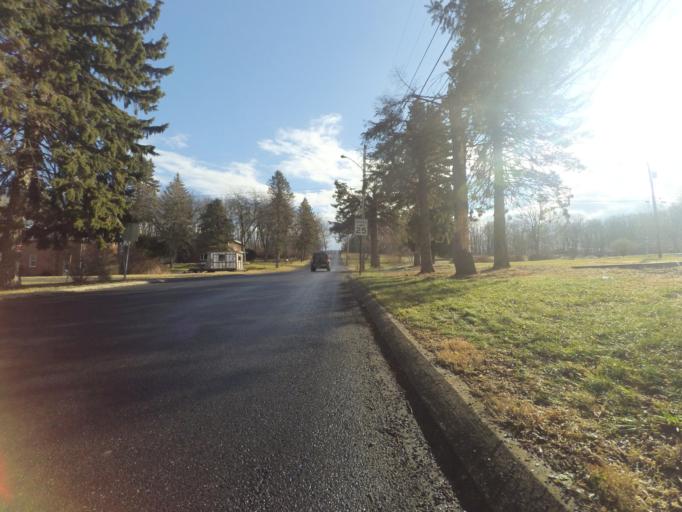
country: US
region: Pennsylvania
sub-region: Centre County
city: Lemont
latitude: 40.8078
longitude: -77.8322
